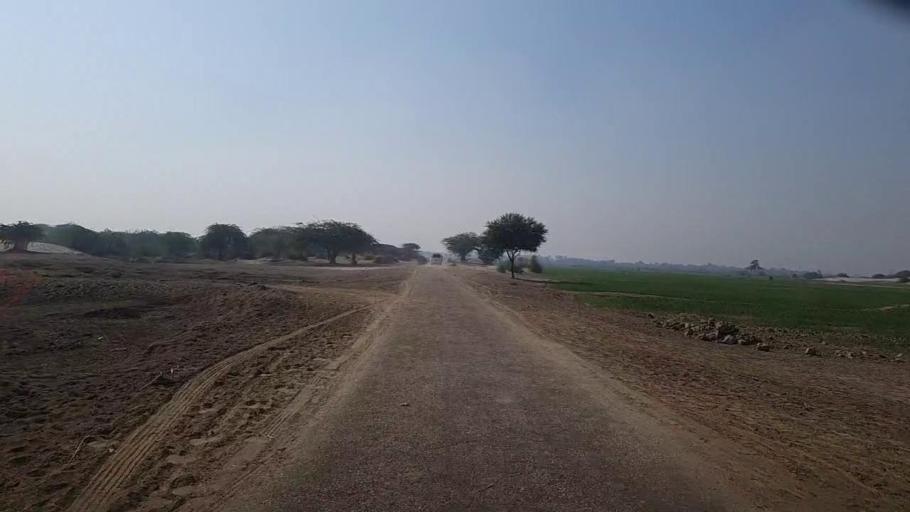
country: PK
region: Sindh
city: Bozdar
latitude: 27.2558
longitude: 68.6148
